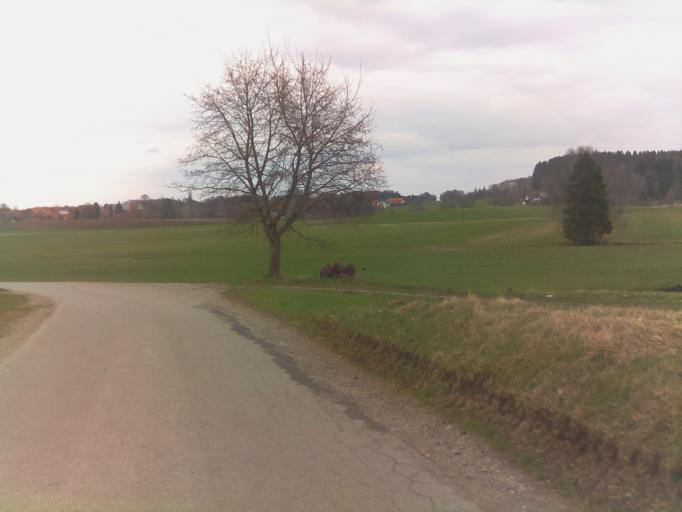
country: DE
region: Bavaria
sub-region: Upper Bavaria
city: Andechs
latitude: 47.9403
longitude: 11.2123
